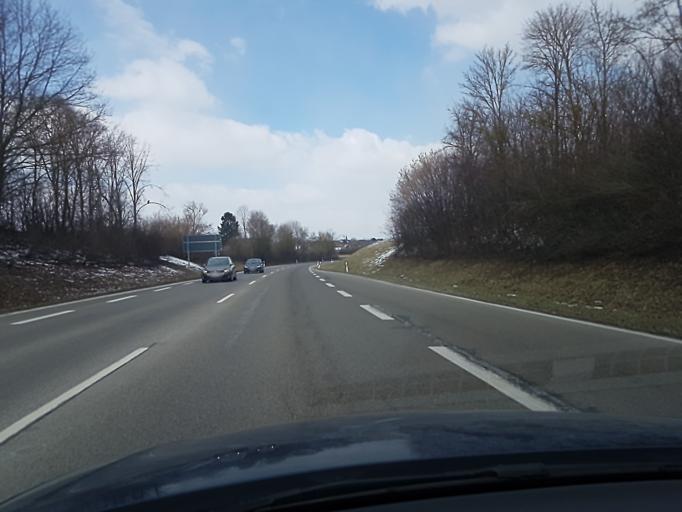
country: DE
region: Baden-Wuerttemberg
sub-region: Regierungsbezirk Stuttgart
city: Bondorf
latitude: 48.5509
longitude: 8.8438
